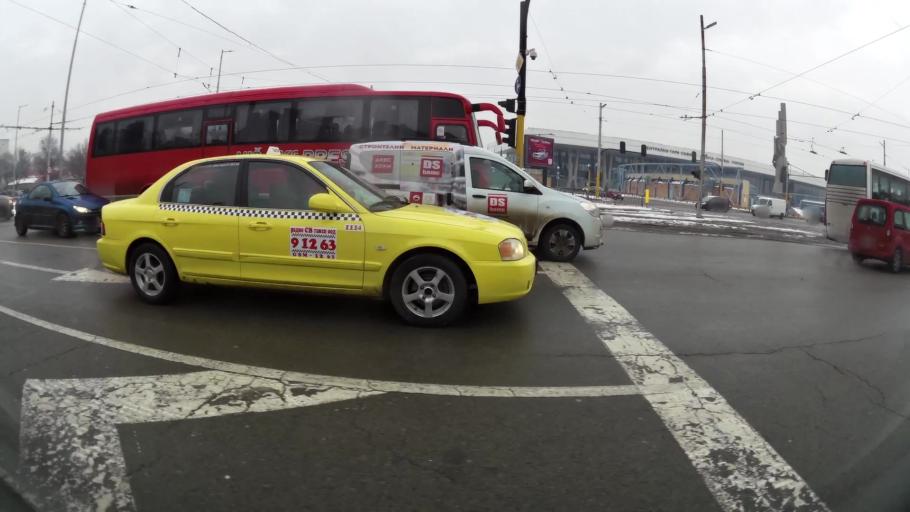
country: BG
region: Sofia-Capital
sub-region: Stolichna Obshtina
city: Sofia
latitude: 42.7114
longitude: 23.3187
